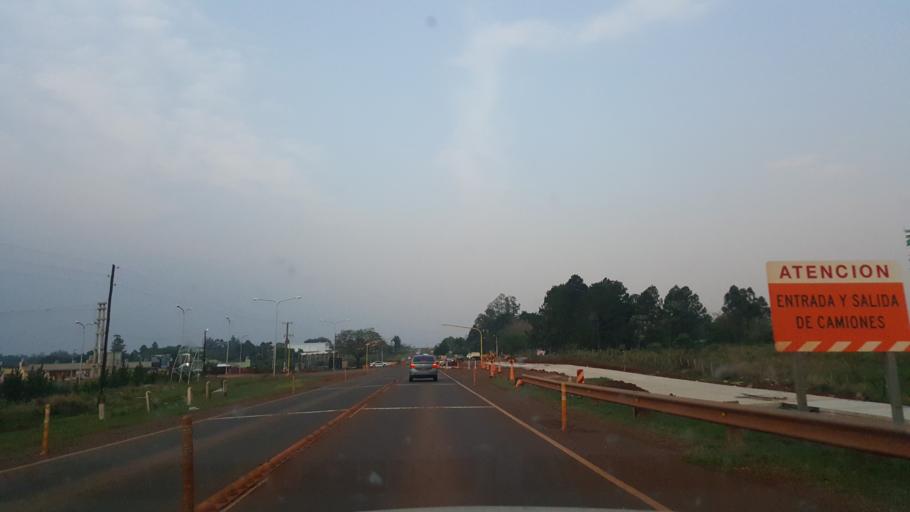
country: AR
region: Misiones
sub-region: Departamento de Capital
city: Posadas
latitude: -27.4117
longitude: -55.9804
